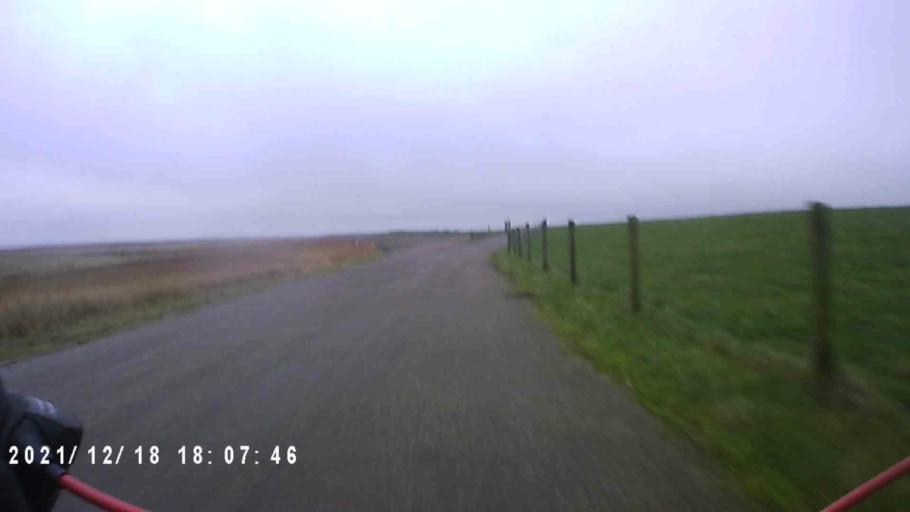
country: NL
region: Friesland
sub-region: Gemeente Dongeradeel
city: Holwerd
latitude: 53.3854
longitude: 5.9195
